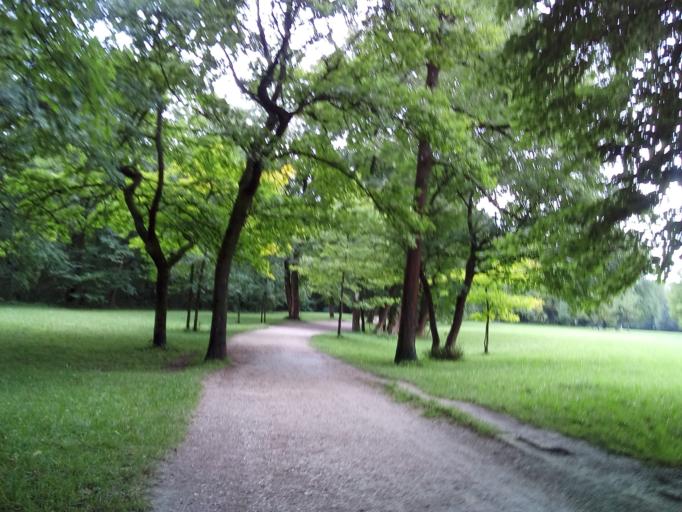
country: DE
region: Bavaria
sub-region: Upper Bavaria
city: Bogenhausen
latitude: 48.1689
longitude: 11.6091
